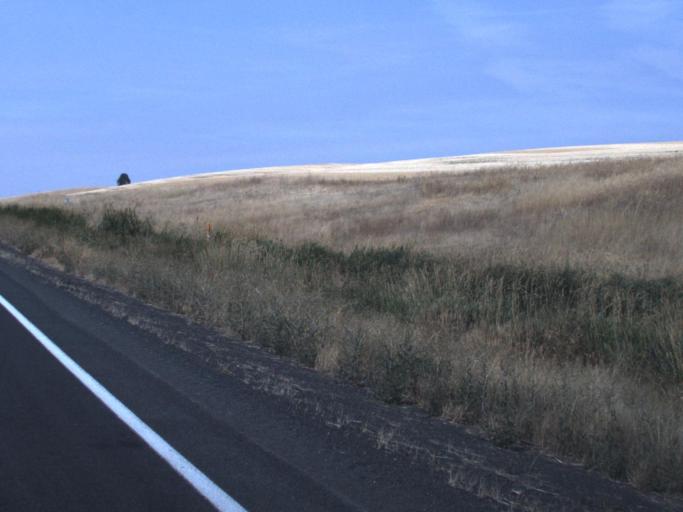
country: US
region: Idaho
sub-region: Latah County
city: Moscow
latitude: 46.9039
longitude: -117.0853
